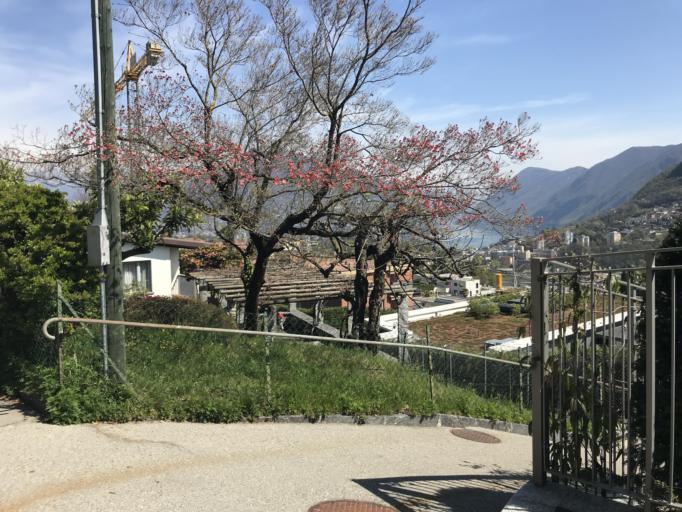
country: CH
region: Ticino
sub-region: Lugano District
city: Montagnola
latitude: 45.9843
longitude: 8.9204
